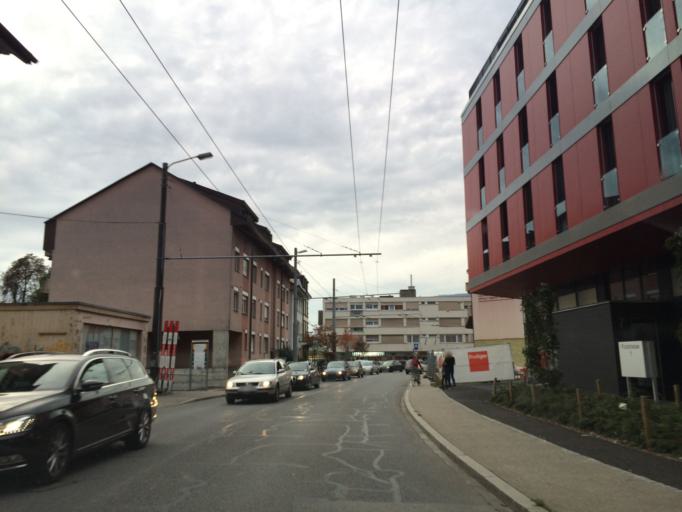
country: CH
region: Bern
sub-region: Biel/Bienne District
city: Brugg
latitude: 47.1461
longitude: 7.2722
